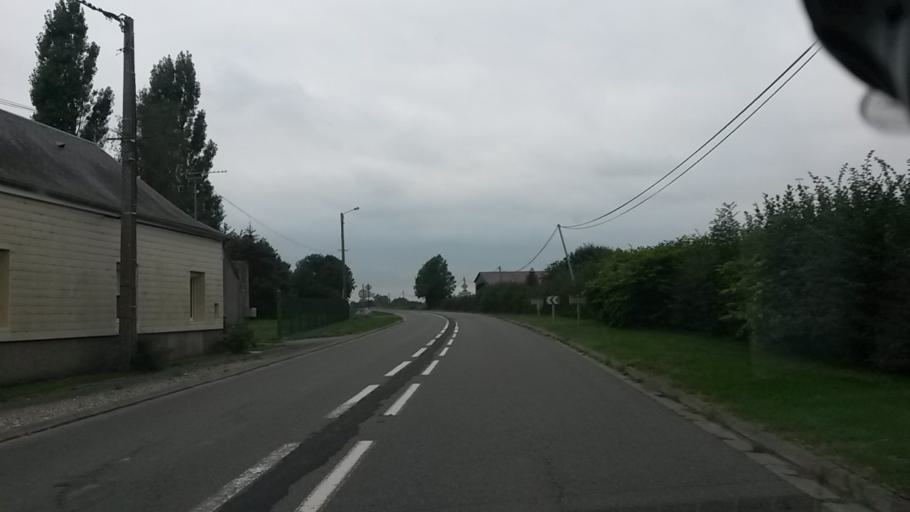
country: FR
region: Picardie
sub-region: Departement de la Somme
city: Hornoy-le-Bourg
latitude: 49.7783
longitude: 1.8849
